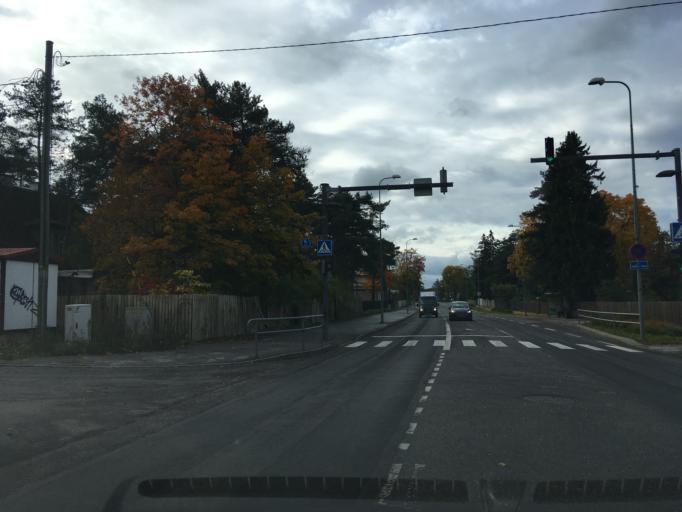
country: EE
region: Harju
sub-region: Saue vald
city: Laagri
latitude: 59.3730
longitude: 24.6438
